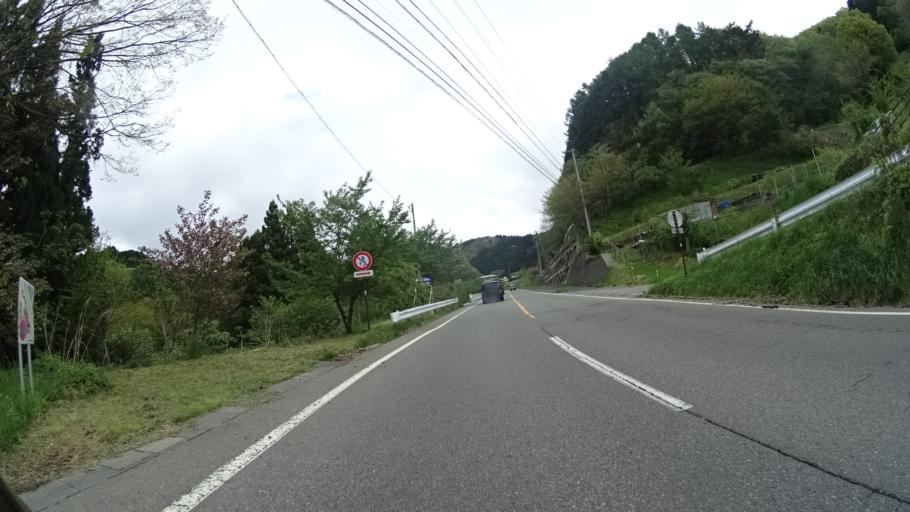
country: JP
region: Nagano
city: Nagano-shi
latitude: 36.7010
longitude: 138.2011
